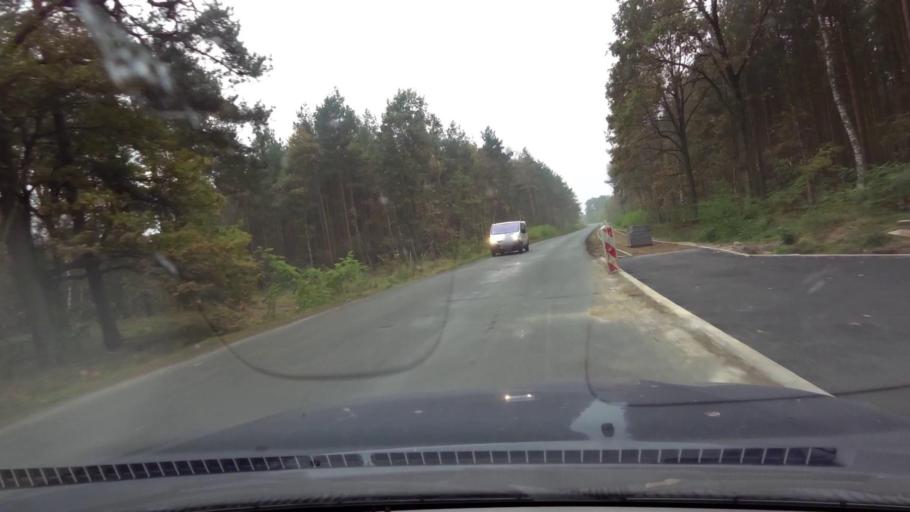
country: PL
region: West Pomeranian Voivodeship
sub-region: Powiat goleniowski
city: Goleniow
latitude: 53.5457
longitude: 14.7728
